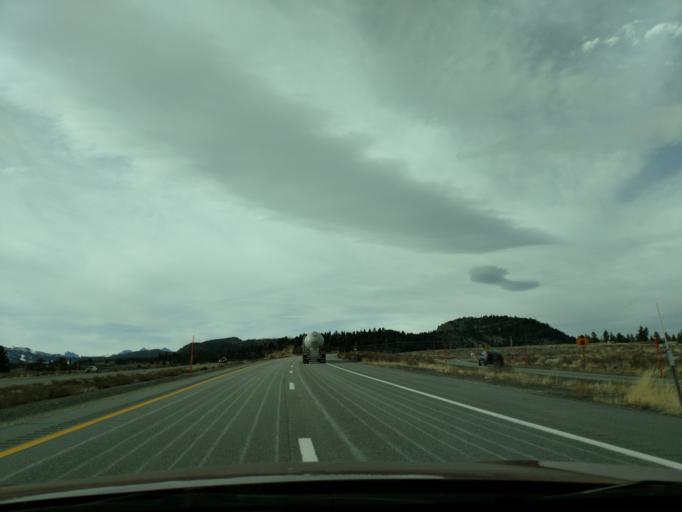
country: US
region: California
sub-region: Mono County
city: Mammoth Lakes
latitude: 37.6398
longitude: -118.9135
